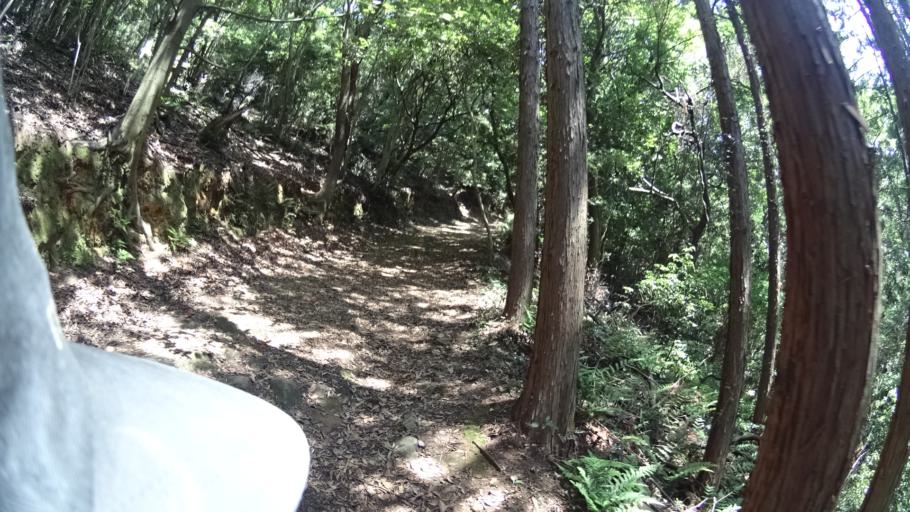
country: JP
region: Shizuoka
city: Kosai-shi
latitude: 34.7391
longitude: 137.4871
